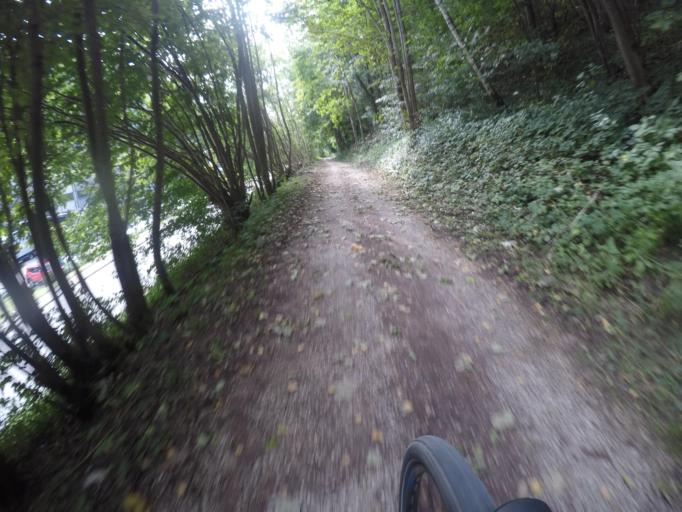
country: DE
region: Baden-Wuerttemberg
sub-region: Tuebingen Region
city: Bad Urach
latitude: 48.4860
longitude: 9.4018
